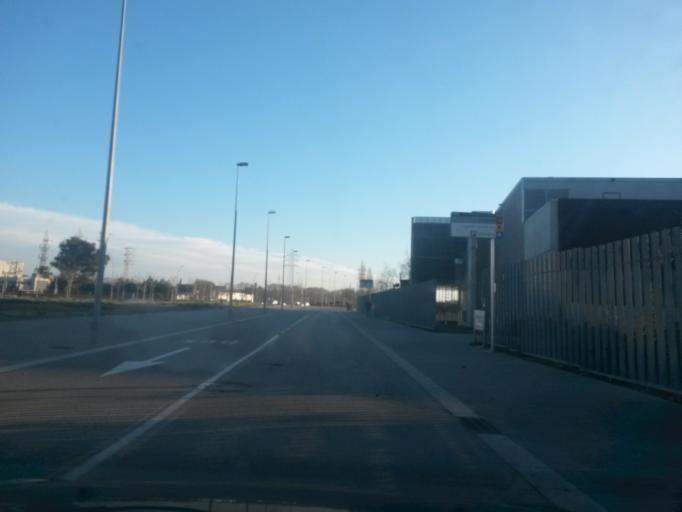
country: ES
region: Catalonia
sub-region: Provincia de Girona
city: Salt
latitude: 41.9705
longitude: 2.7984
